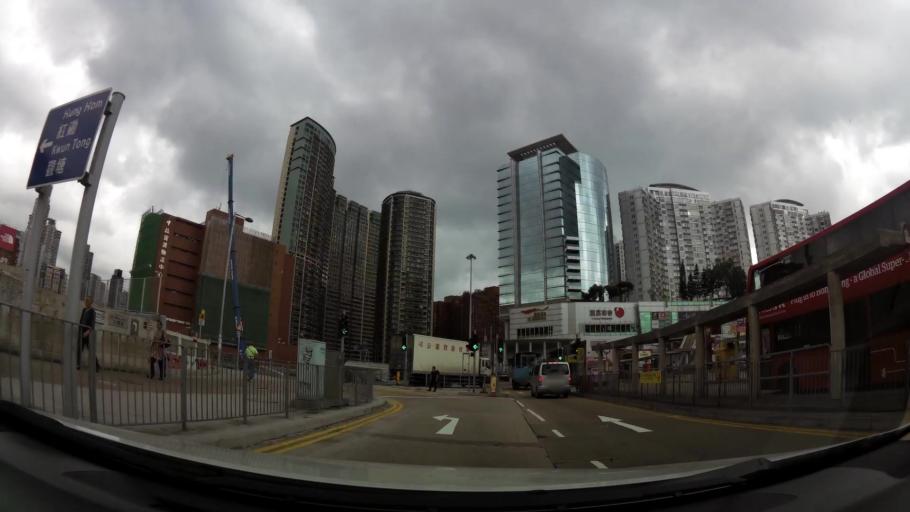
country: HK
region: Kowloon City
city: Kowloon
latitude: 22.3042
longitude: 114.1818
